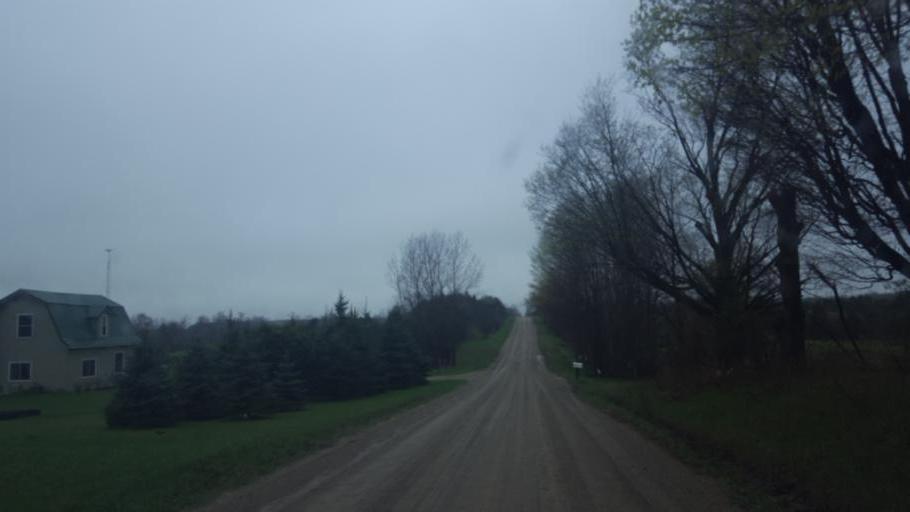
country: US
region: Michigan
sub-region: Isabella County
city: Lake Isabella
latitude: 43.5818
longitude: -85.0069
